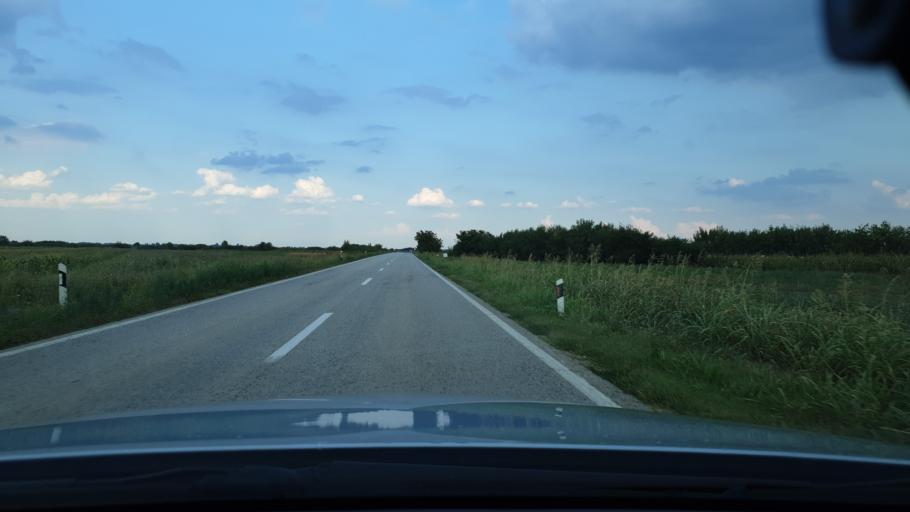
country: RS
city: Konak
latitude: 45.3297
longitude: 20.8863
